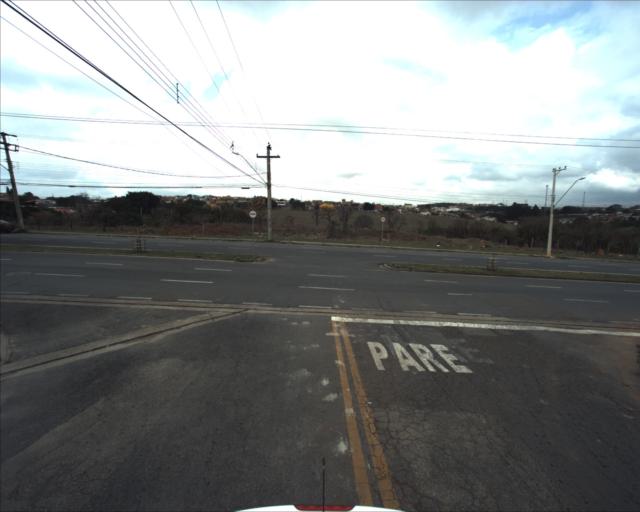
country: BR
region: Sao Paulo
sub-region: Sorocaba
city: Sorocaba
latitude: -23.4364
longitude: -47.5105
